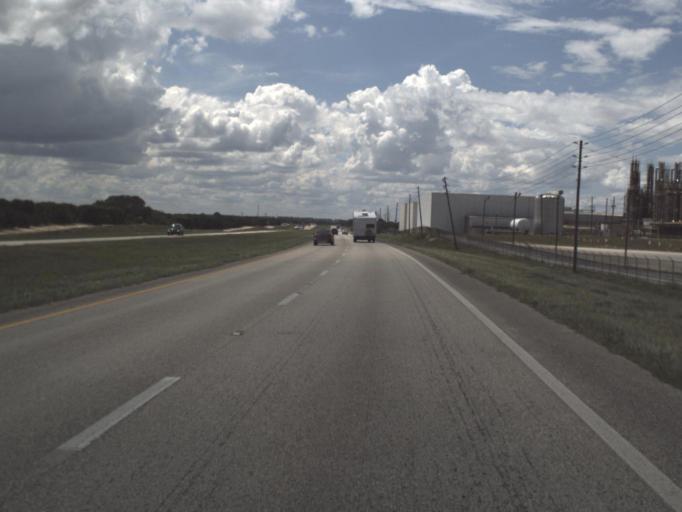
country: US
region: Florida
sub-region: Polk County
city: Babson Park
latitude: 27.8943
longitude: -81.4874
